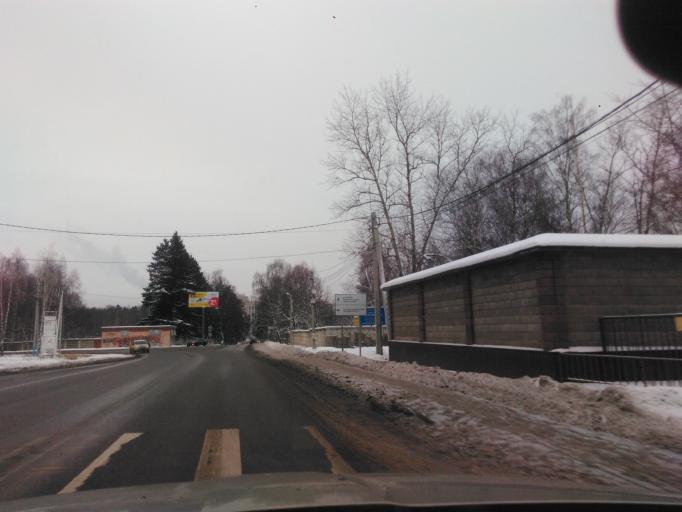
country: RU
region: Moskovskaya
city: Andreyevka
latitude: 55.9810
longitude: 37.1209
